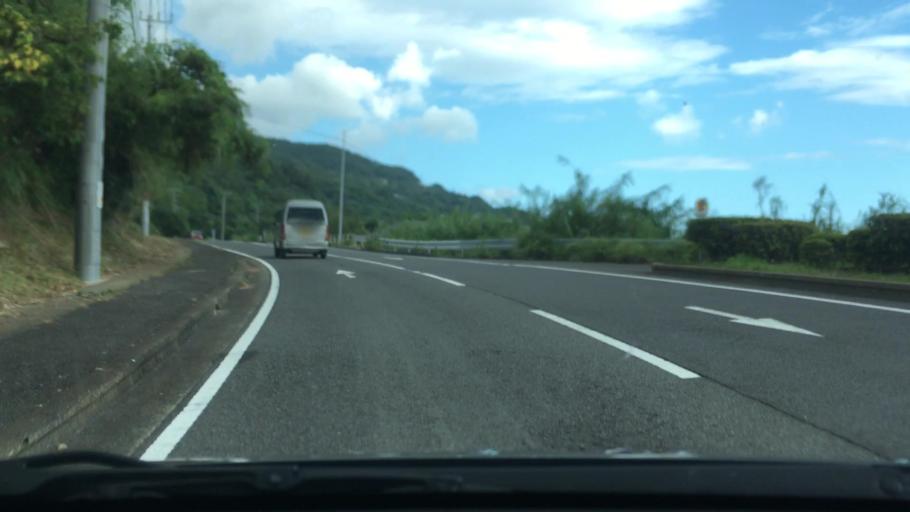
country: JP
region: Nagasaki
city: Togitsu
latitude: 32.8690
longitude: 129.6790
